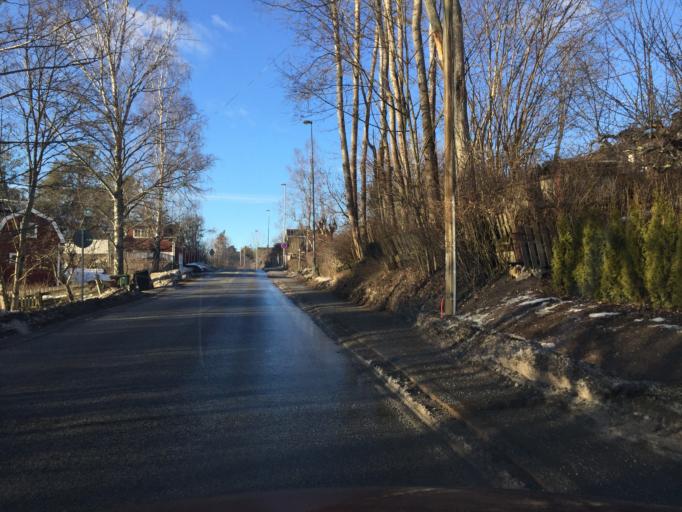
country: SE
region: Stockholm
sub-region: Salems Kommun
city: Ronninge
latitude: 59.1977
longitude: 17.7437
